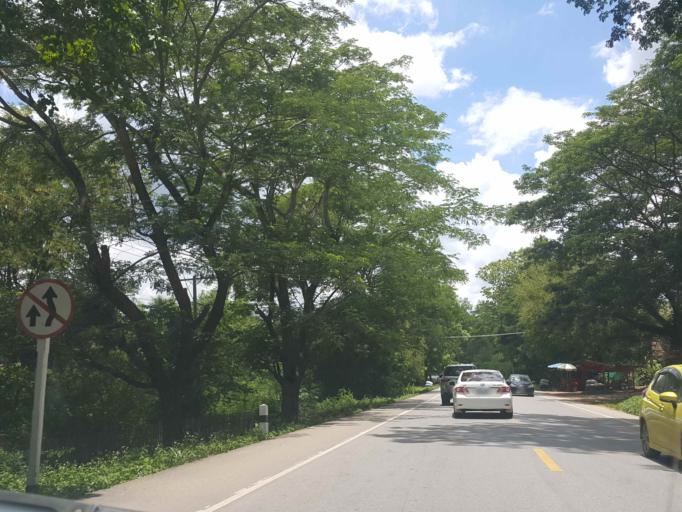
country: TH
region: Nan
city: Wiang Sa
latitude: 18.5167
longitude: 100.5970
